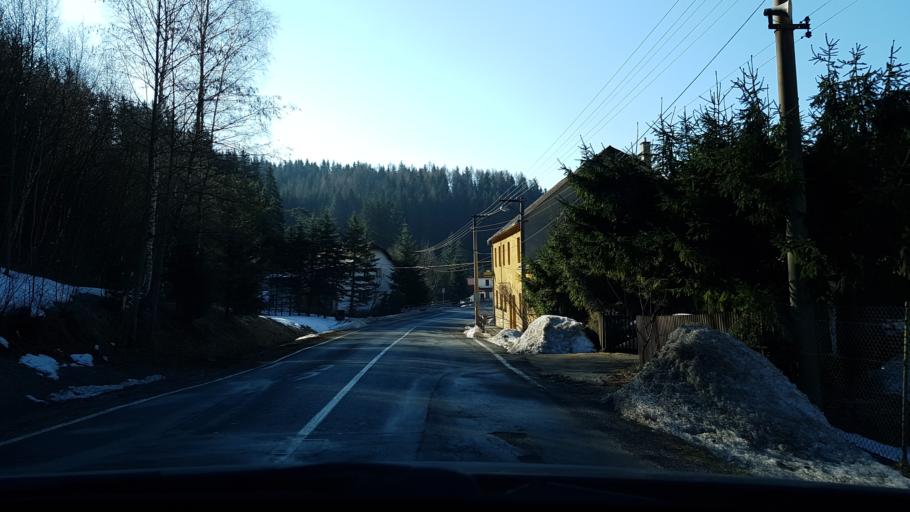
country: CZ
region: Olomoucky
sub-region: Okres Sumperk
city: Stare Mesto
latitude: 50.1139
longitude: 17.0053
